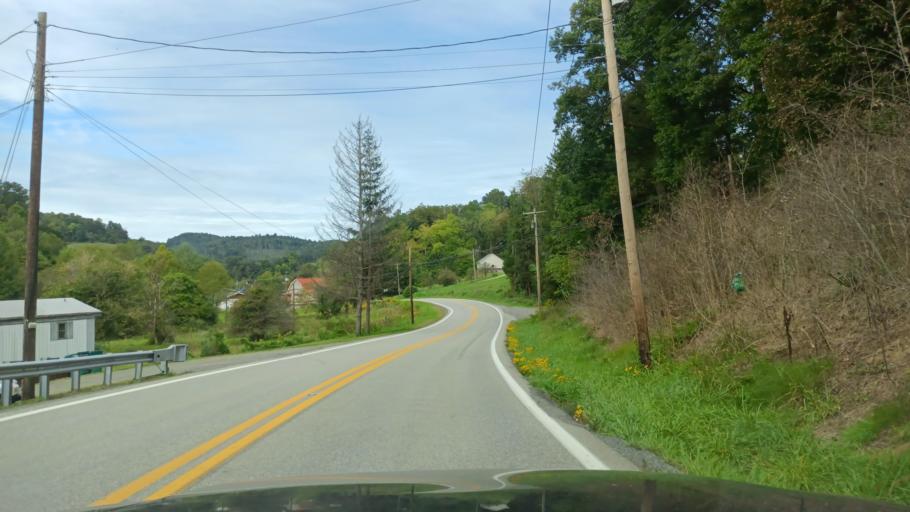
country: US
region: West Virginia
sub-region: Taylor County
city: Grafton
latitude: 39.3281
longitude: -80.1019
